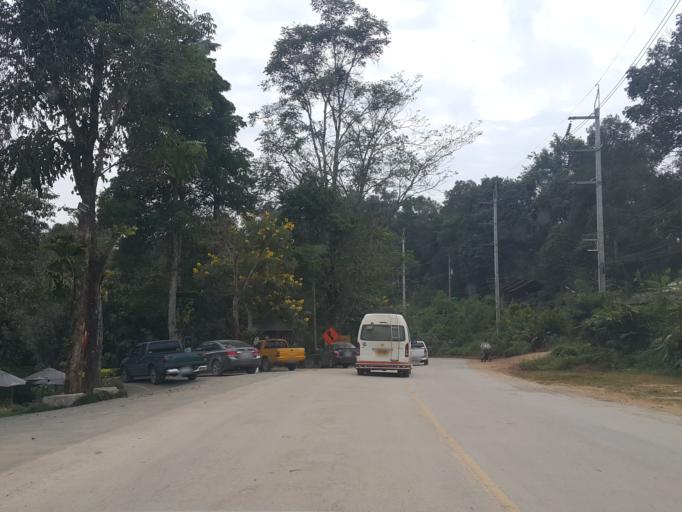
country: TH
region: Chiang Mai
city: Mae Taeng
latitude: 19.1330
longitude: 98.7038
